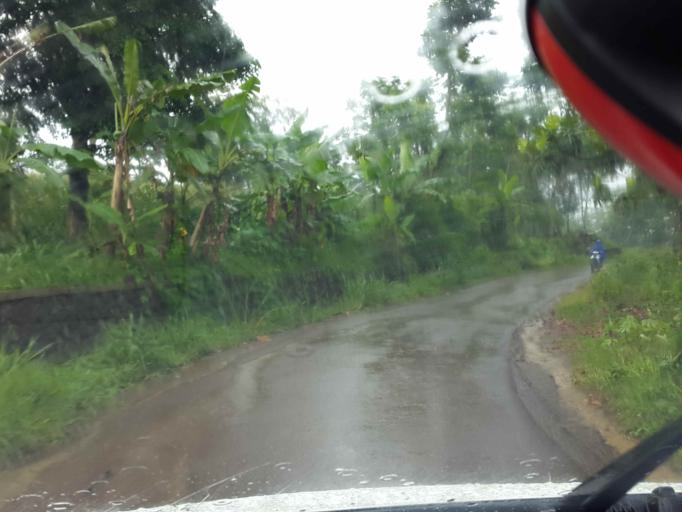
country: ID
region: West Java
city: Cilandak
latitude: -6.9866
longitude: 106.7148
